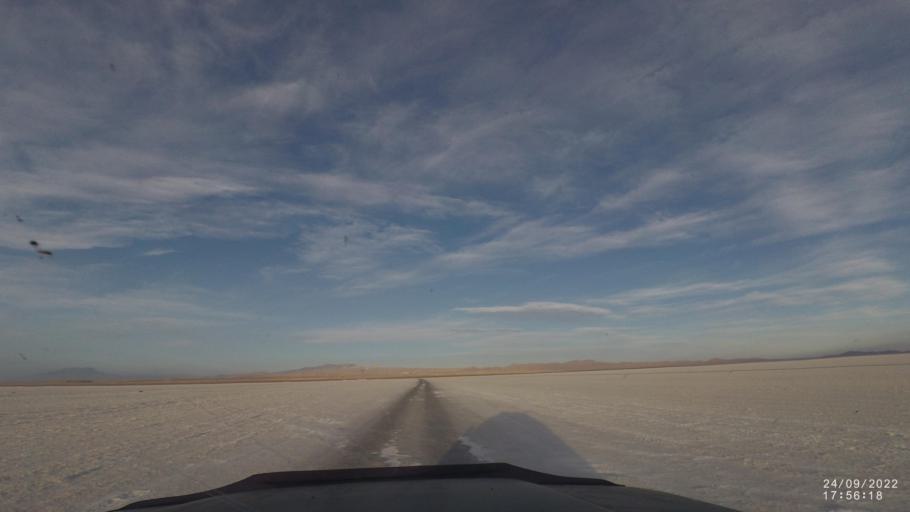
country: BO
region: Potosi
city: Colchani
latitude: -20.3246
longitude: -67.0151
